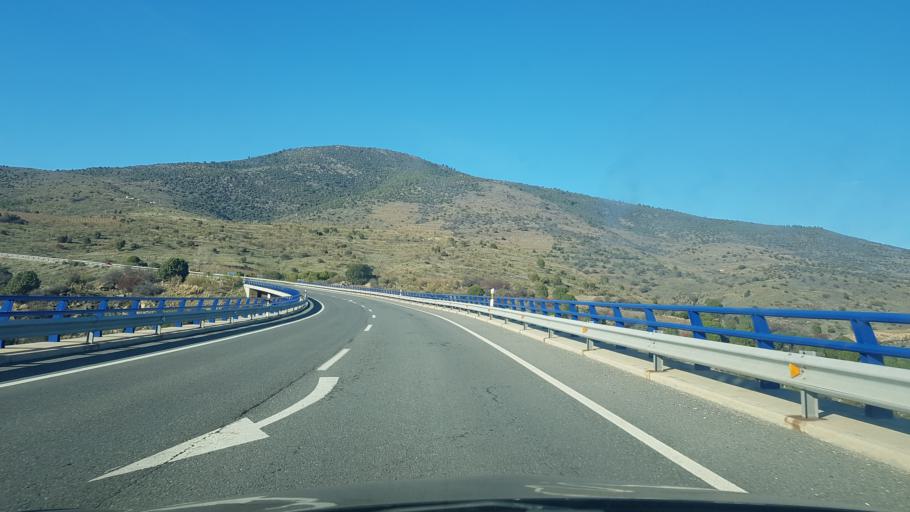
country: ES
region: Castille and Leon
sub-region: Provincia de Avila
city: El Tiemblo
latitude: 40.4286
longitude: -4.4972
